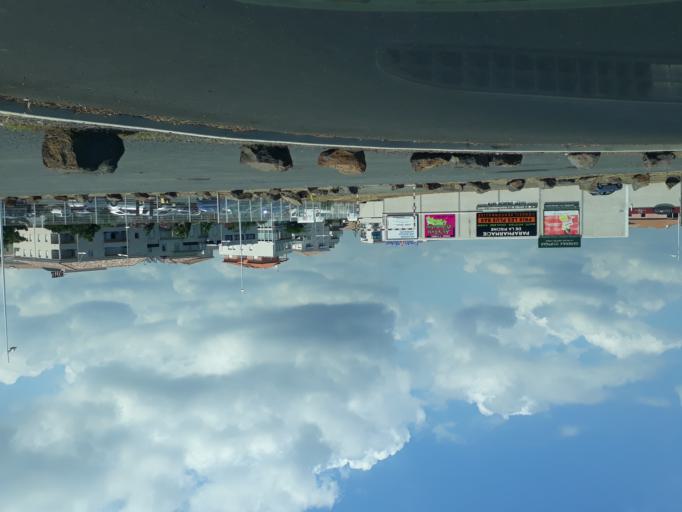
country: FR
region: Languedoc-Roussillon
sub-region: Departement de l'Herault
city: Agde
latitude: 43.2987
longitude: 3.4722
